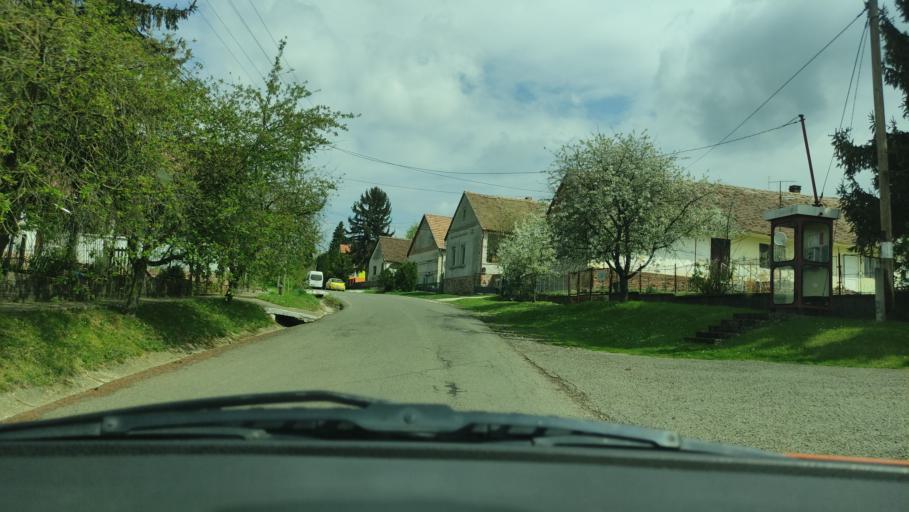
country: HU
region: Baranya
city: Sasd
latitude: 46.2904
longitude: 18.1028
